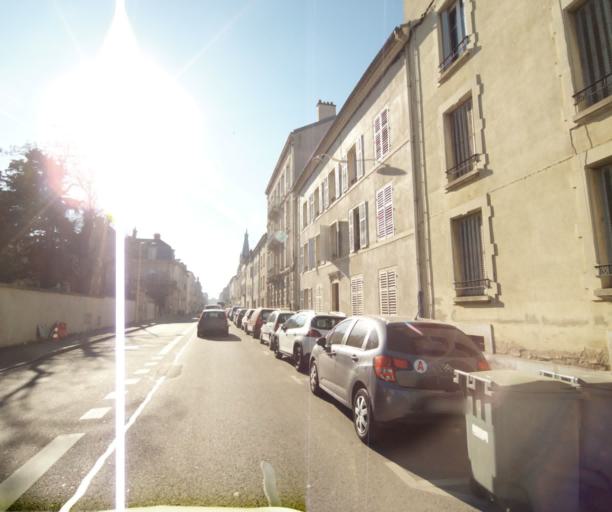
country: FR
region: Lorraine
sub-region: Departement de Meurthe-et-Moselle
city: Maxeville
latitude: 48.7026
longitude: 6.1708
